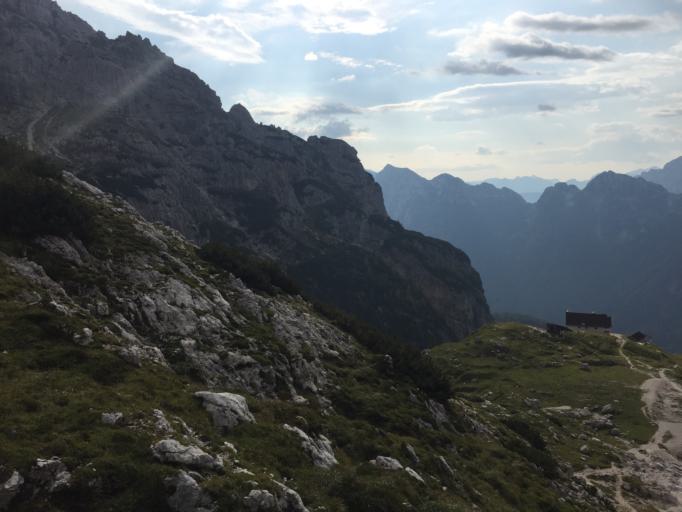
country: IT
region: Friuli Venezia Giulia
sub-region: Provincia di Udine
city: Malborghetto
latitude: 46.4238
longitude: 13.4978
